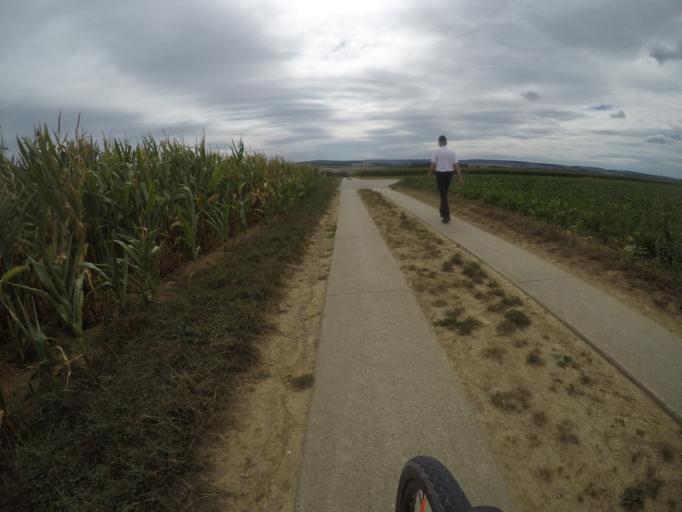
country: DE
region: Baden-Wuerttemberg
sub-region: Regierungsbezirk Stuttgart
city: Vaihingen an der Enz
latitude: 48.9370
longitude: 8.9928
